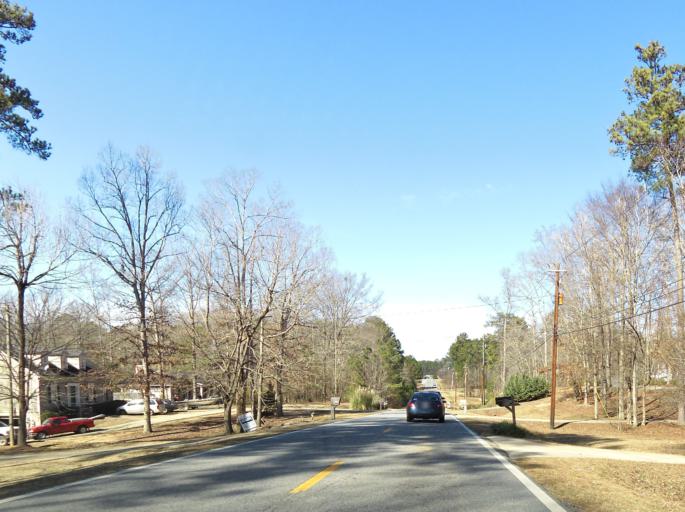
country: US
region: Georgia
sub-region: Bibb County
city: West Point
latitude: 32.8652
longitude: -83.7556
